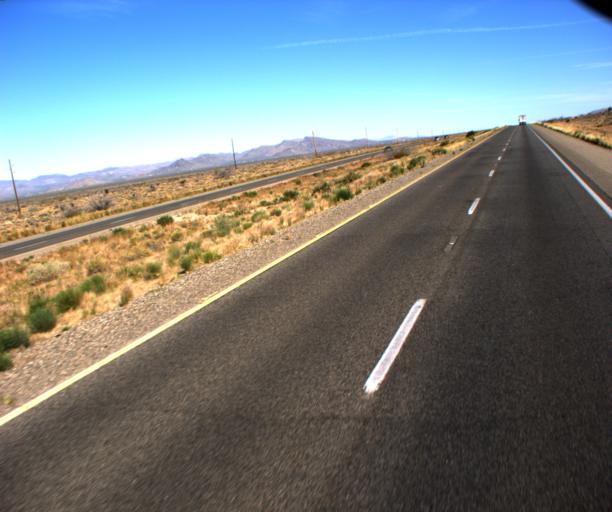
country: US
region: Arizona
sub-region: Mohave County
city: Golden Valley
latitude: 35.2667
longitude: -114.1648
